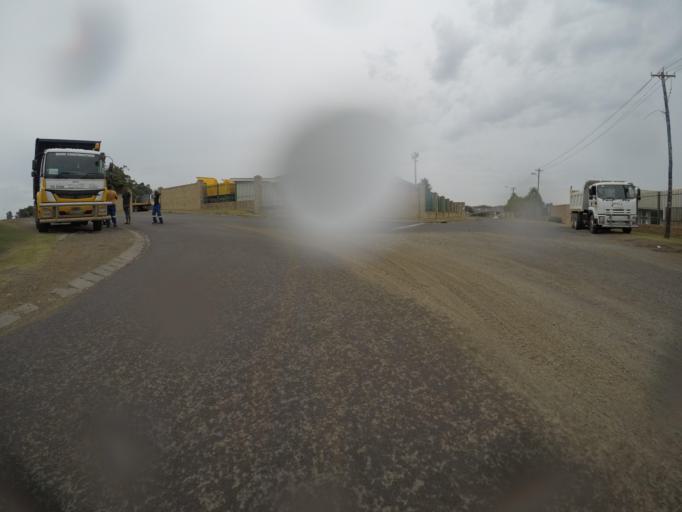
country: ZA
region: Eastern Cape
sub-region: Buffalo City Metropolitan Municipality
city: East London
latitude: -32.9779
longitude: 27.8236
